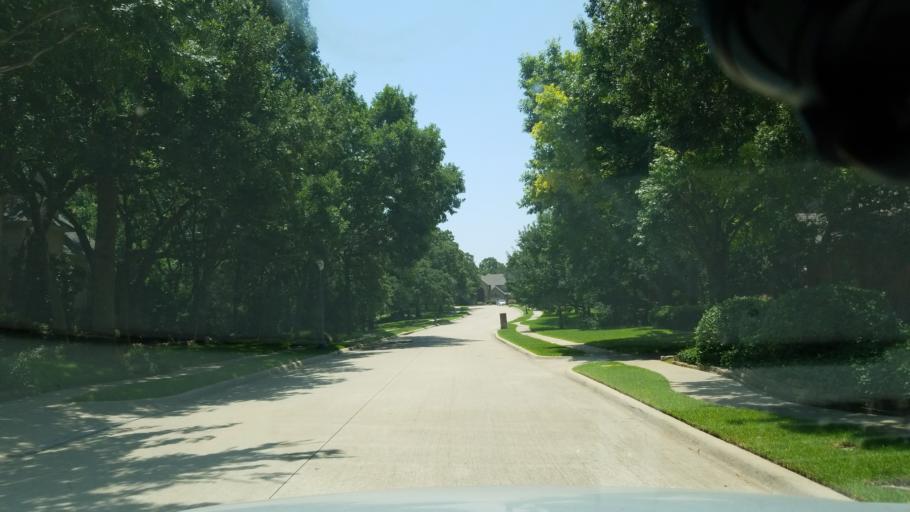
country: US
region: Texas
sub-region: Dallas County
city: Coppell
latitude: 32.9591
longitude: -96.9955
